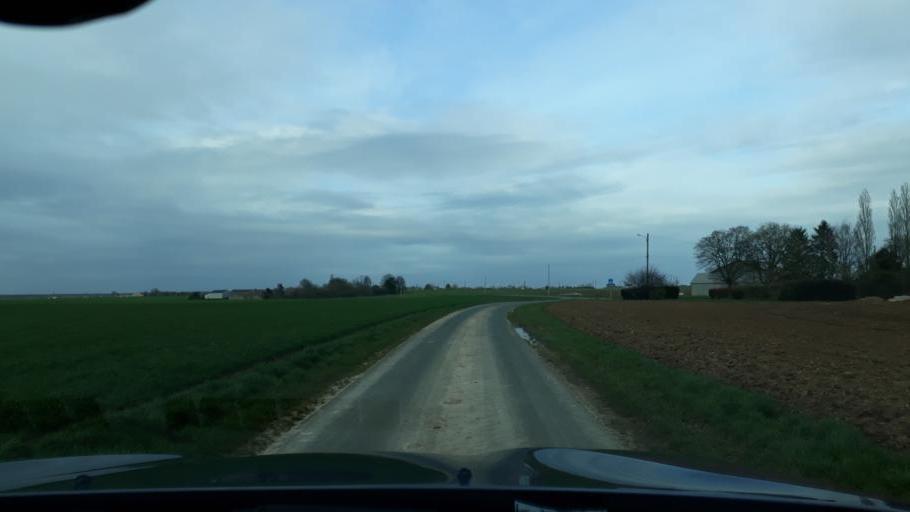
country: FR
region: Centre
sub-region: Departement du Loir-et-Cher
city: Mer
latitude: 47.7867
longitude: 1.4834
